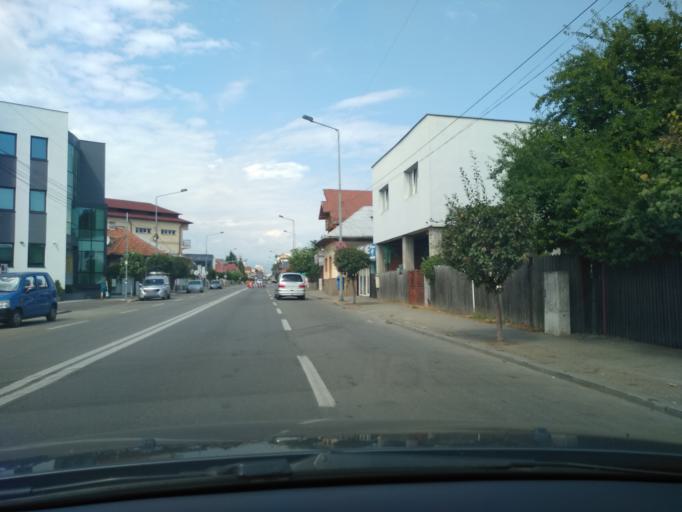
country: RO
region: Gorj
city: Targu Jiu
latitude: 45.0286
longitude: 23.2691
